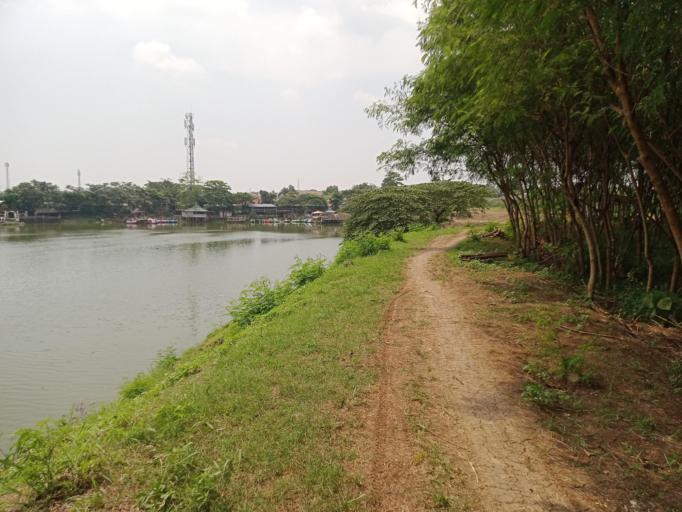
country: ID
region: West Java
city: Pasarkemis
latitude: -6.1745
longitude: 106.5392
